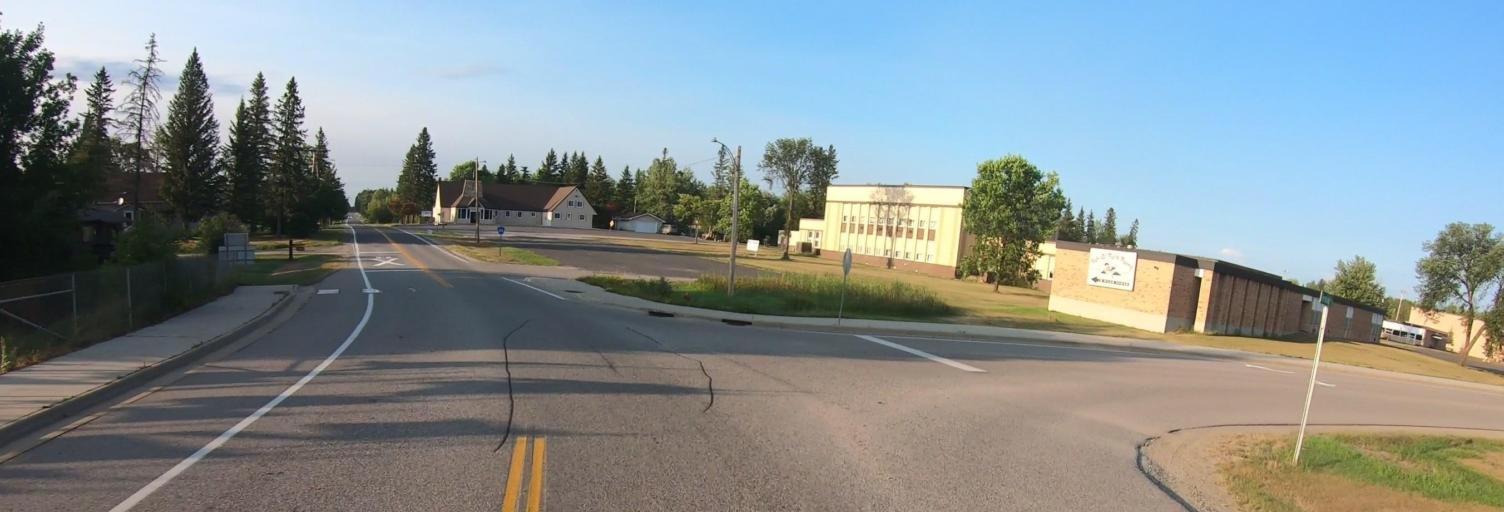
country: US
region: Minnesota
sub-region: Saint Louis County
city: Mountain Iron
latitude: 47.8539
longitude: -92.6827
